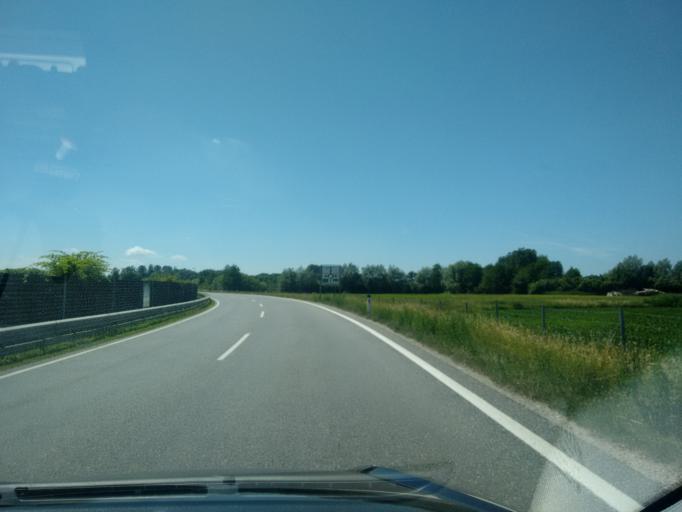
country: AT
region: Lower Austria
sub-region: Politischer Bezirk Sankt Polten
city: Prinzersdorf
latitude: 48.2094
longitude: 15.5119
